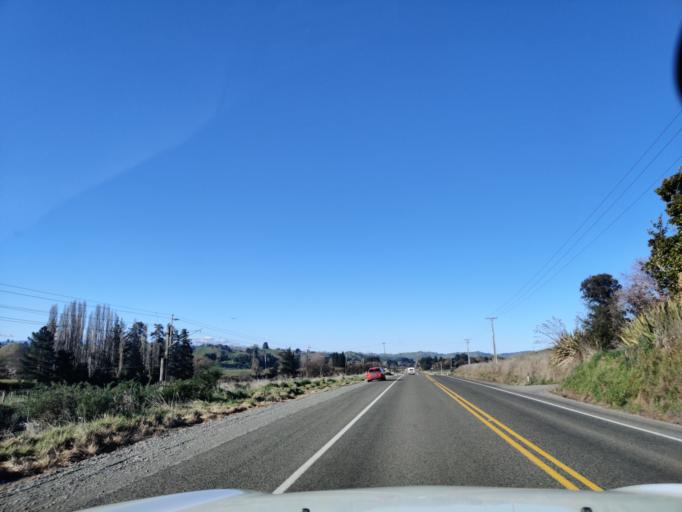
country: NZ
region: Manawatu-Wanganui
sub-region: Ruapehu District
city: Waiouru
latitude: -39.7157
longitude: 175.8394
